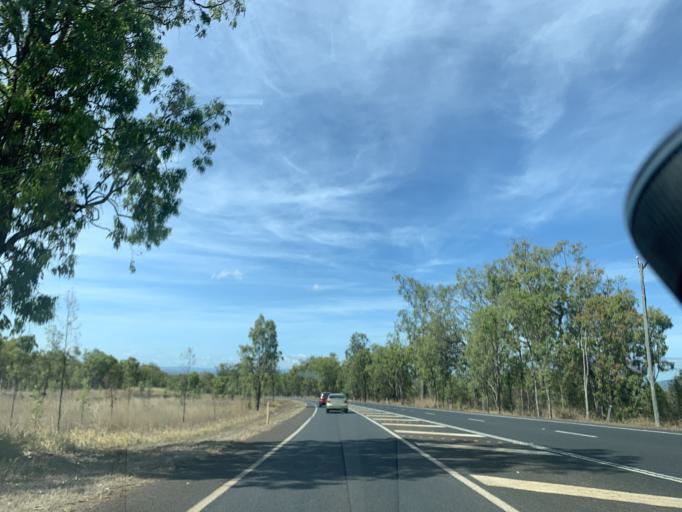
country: AU
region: Queensland
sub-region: Tablelands
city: Mareeba
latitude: -17.1028
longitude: 145.4367
